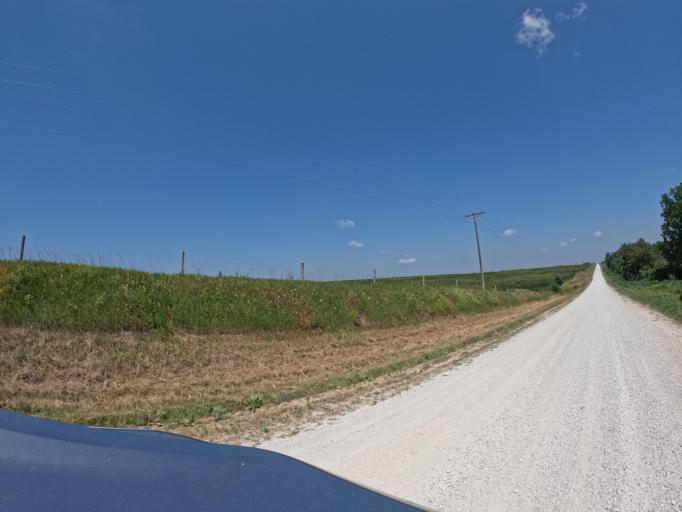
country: US
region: Iowa
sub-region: Keokuk County
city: Sigourney
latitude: 41.2696
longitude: -92.2381
